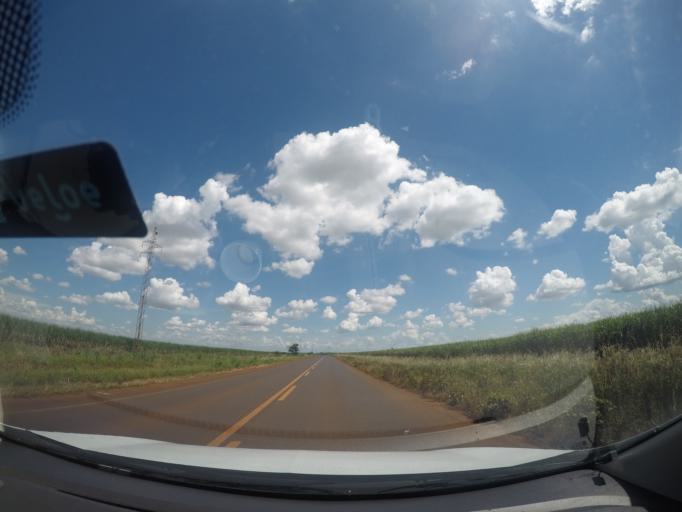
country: BR
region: Minas Gerais
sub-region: Frutal
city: Frutal
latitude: -19.8214
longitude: -48.7321
